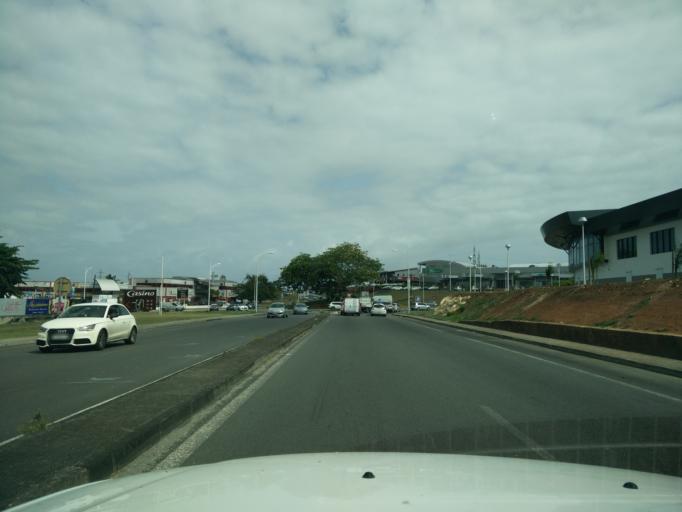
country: GP
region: Guadeloupe
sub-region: Guadeloupe
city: Baie-Mahault
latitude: 16.2412
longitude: -61.5715
